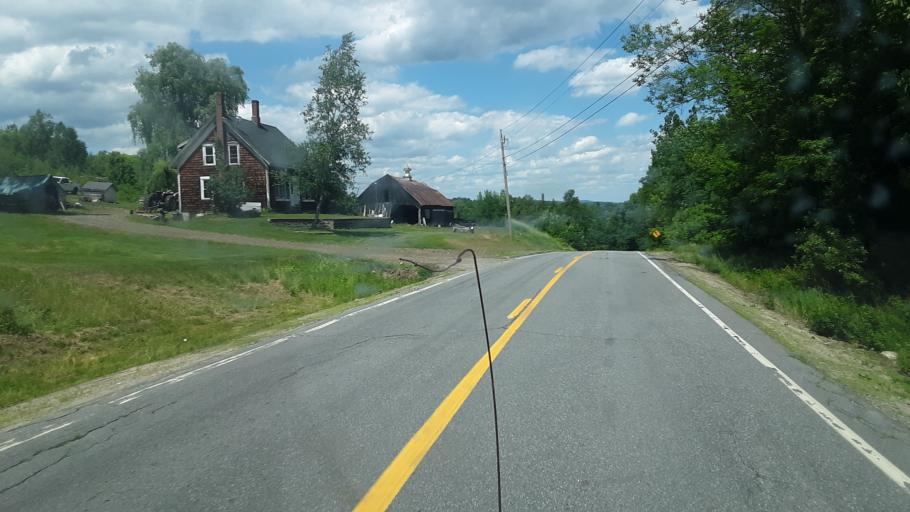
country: US
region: Maine
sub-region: Franklin County
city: Chesterville
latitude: 44.5835
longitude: -70.1528
